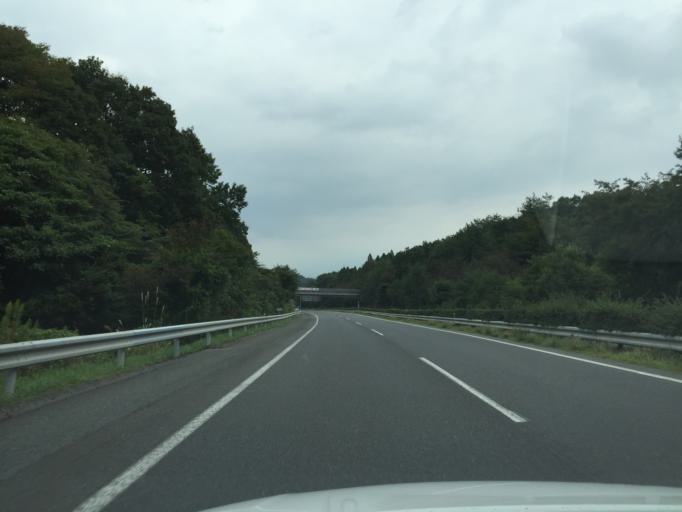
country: JP
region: Fukushima
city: Iwaki
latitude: 37.0418
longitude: 140.8199
